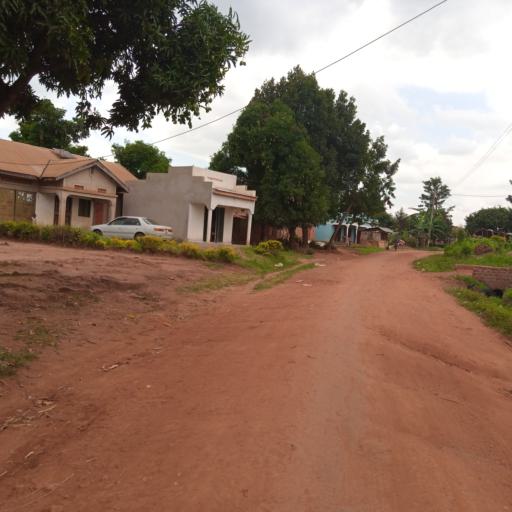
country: UG
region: Eastern Region
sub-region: Mbale District
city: Mbale
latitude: 1.1185
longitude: 34.1767
